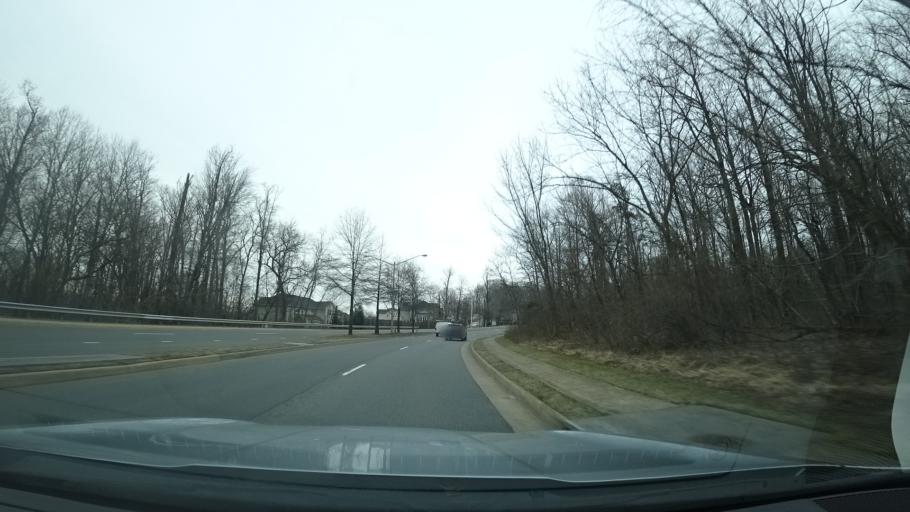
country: US
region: Virginia
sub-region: Fairfax County
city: Herndon
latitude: 38.9822
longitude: -77.3872
